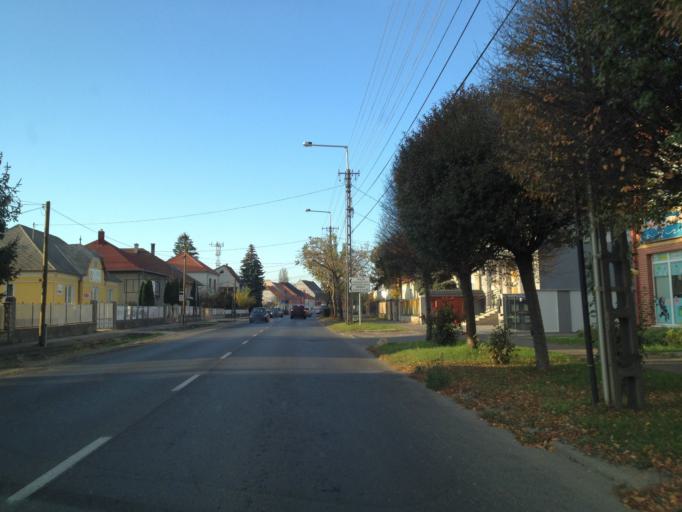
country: HU
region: Gyor-Moson-Sopron
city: Gyor
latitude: 47.6609
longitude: 17.6525
